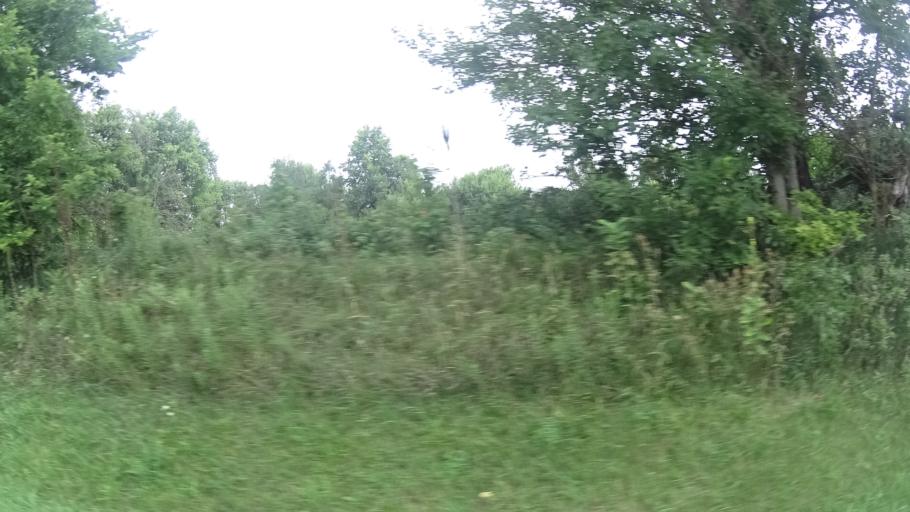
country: US
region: Indiana
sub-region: Madison County
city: Pendleton
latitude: 40.0031
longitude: -85.7590
